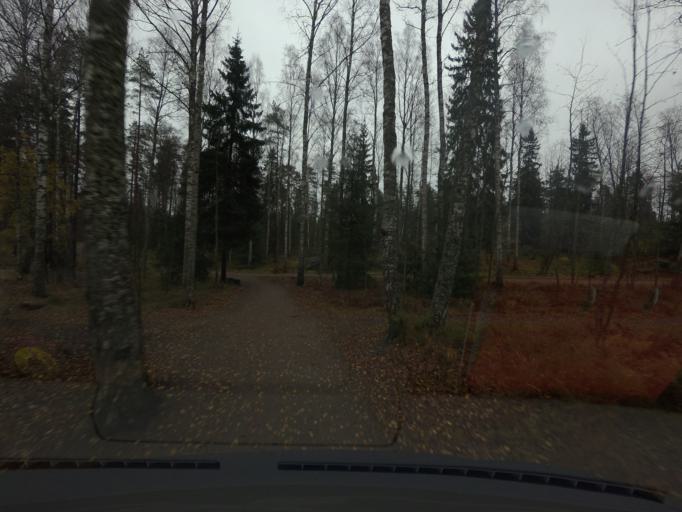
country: FI
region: Uusimaa
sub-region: Helsinki
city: Kauniainen
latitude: 60.2280
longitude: 24.7508
